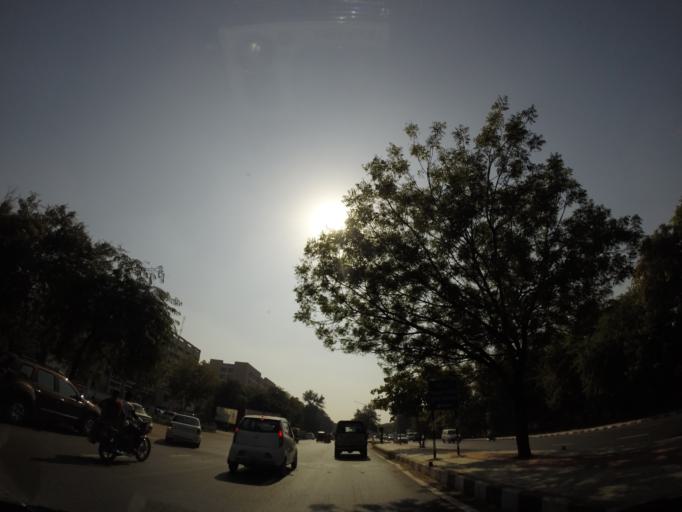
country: IN
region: Gujarat
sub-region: Gandhinagar
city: Ghandinagar
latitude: 23.2200
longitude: 72.6433
